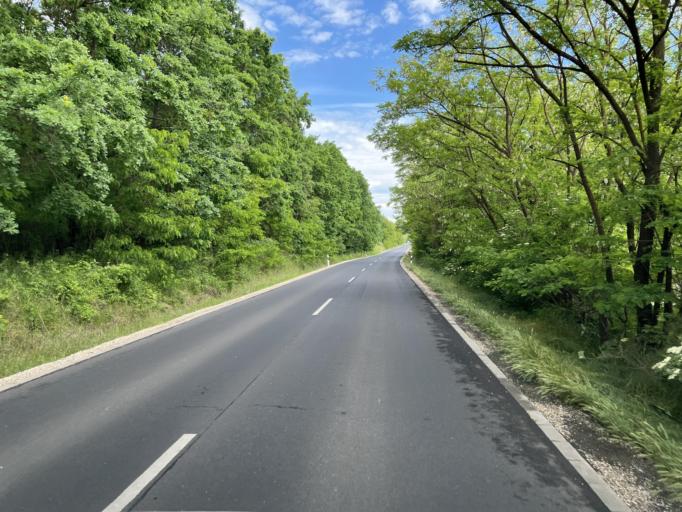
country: HU
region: Pest
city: Pecel
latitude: 47.5111
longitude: 19.3698
